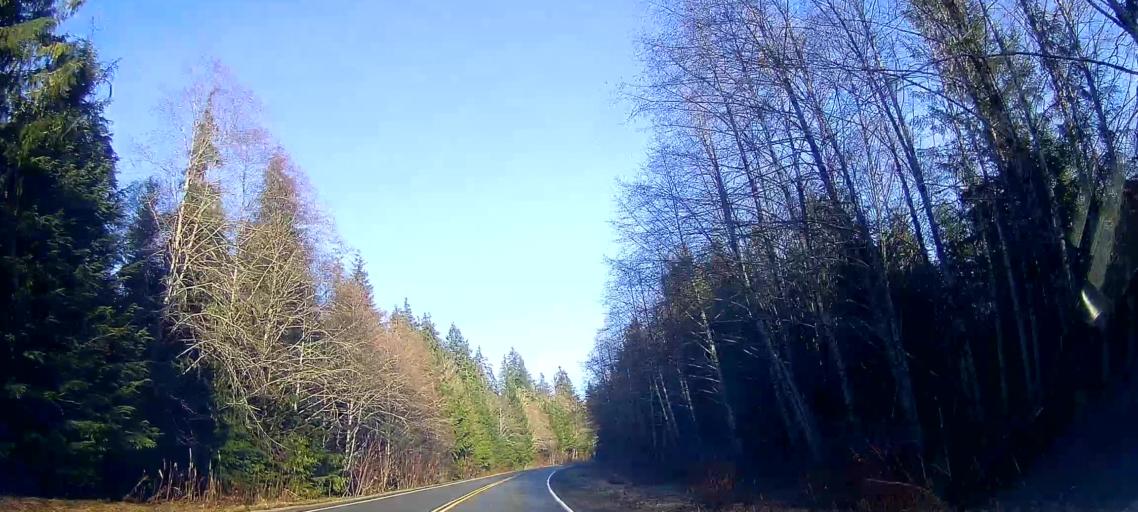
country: US
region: Washington
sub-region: Snohomish County
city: Darrington
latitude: 48.6402
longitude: -121.7339
